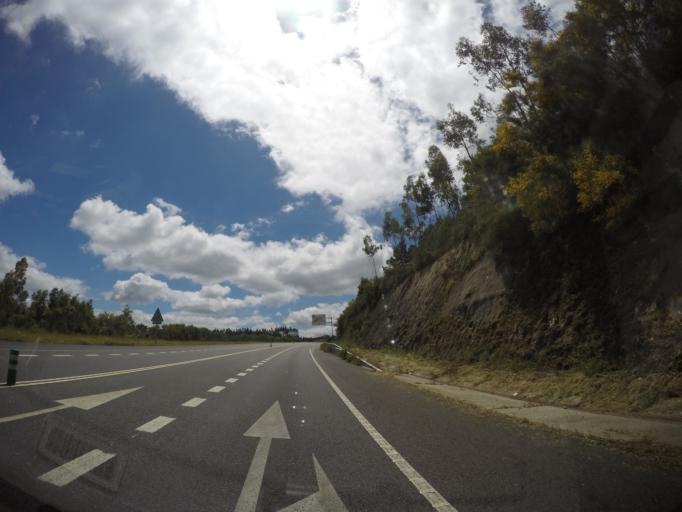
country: ES
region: Aragon
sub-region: Provincia de Zaragoza
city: Fuentes de Ebro
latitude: 41.4997
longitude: -0.6644
